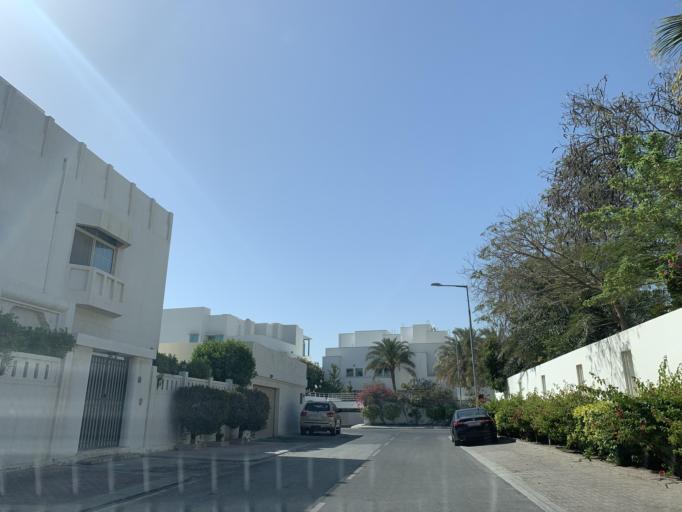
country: BH
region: Manama
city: Manama
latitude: 26.2009
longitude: 50.5701
